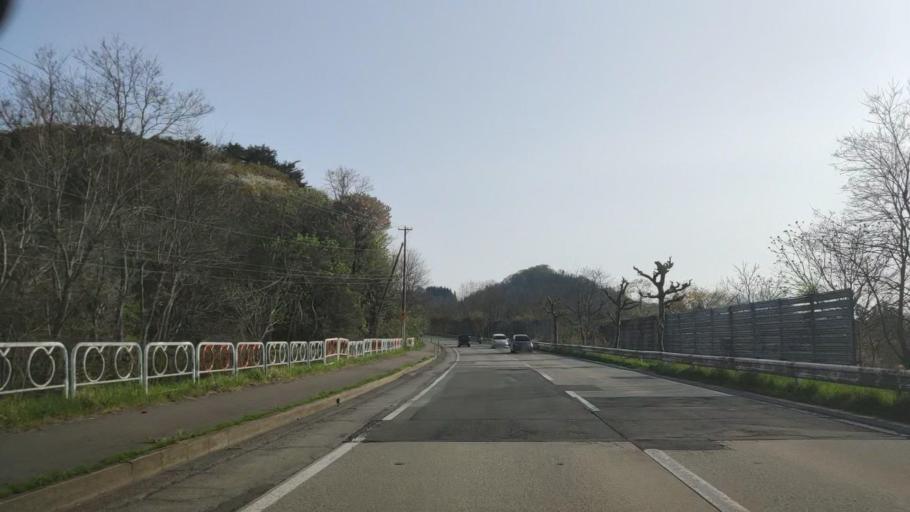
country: JP
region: Aomori
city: Aomori Shi
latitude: 40.8676
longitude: 140.8471
